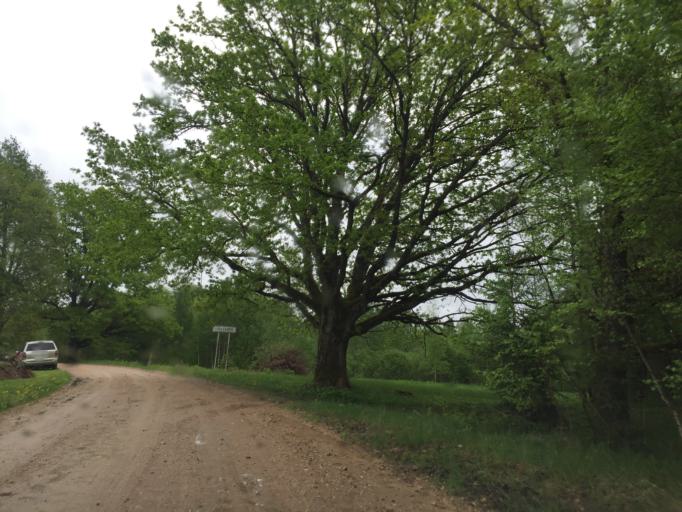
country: LV
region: Lielvarde
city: Lielvarde
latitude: 56.7274
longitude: 24.7724
